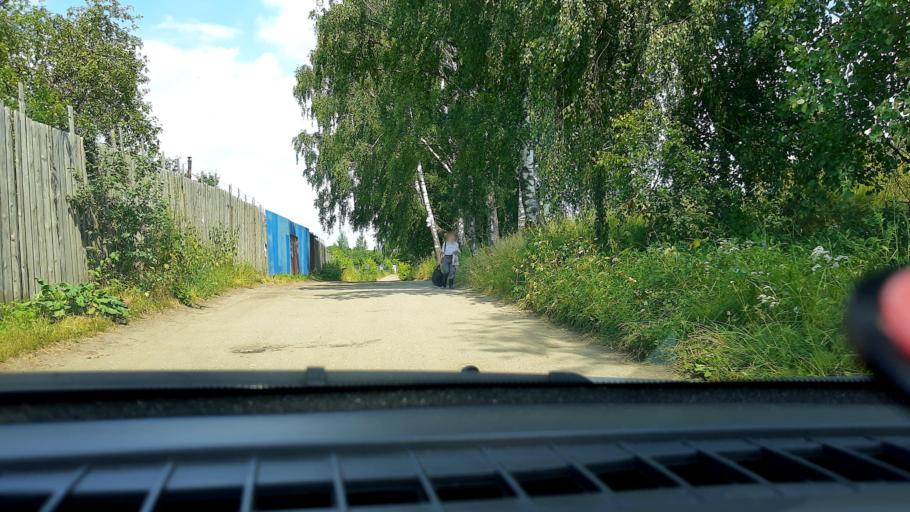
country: RU
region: Nizjnij Novgorod
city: Neklyudovo
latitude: 56.4482
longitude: 44.0042
